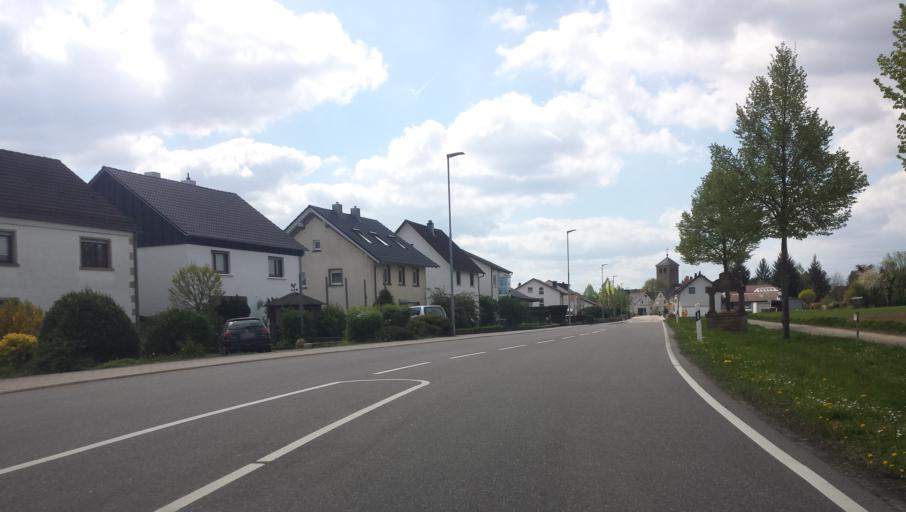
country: DE
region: Baden-Wuerttemberg
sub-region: Karlsruhe Region
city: Sinsheim
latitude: 49.1982
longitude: 8.8655
